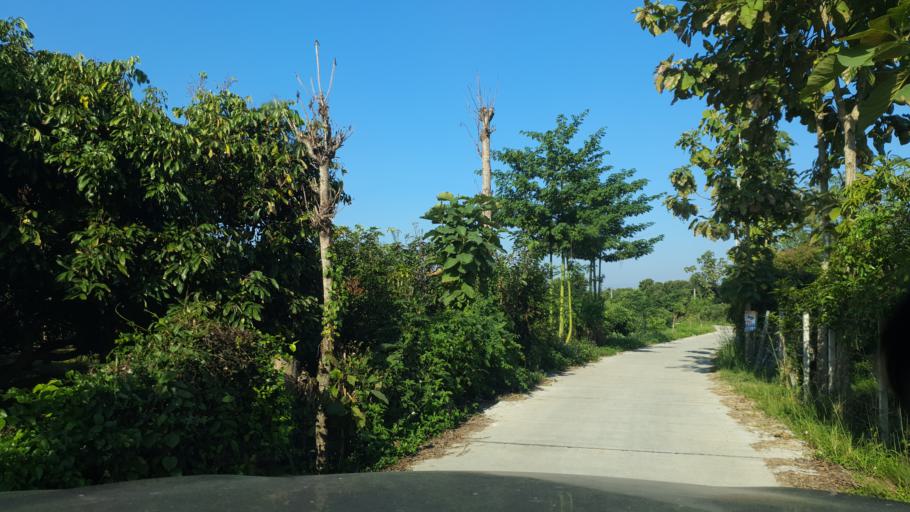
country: TH
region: Chiang Mai
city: San Kamphaeng
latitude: 18.6903
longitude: 99.1462
